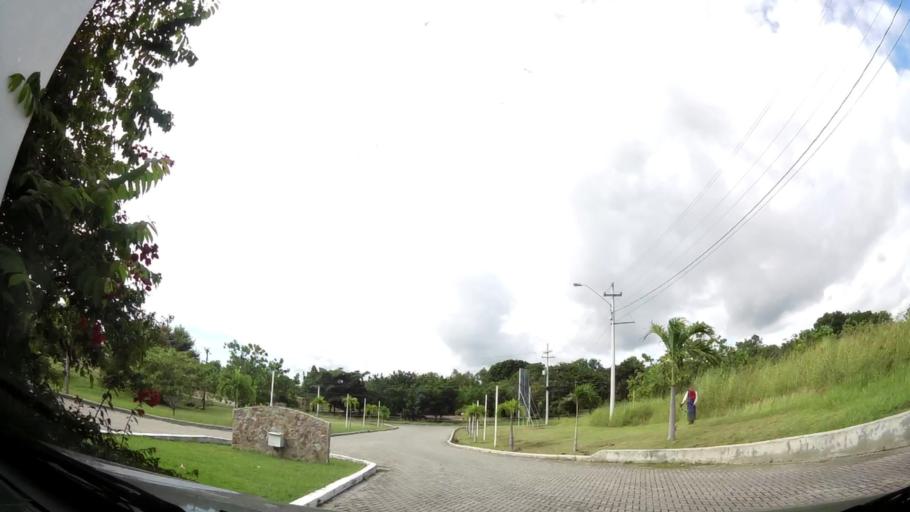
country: PA
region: Panama
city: Nueva Gorgona
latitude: 8.5419
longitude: -79.8989
